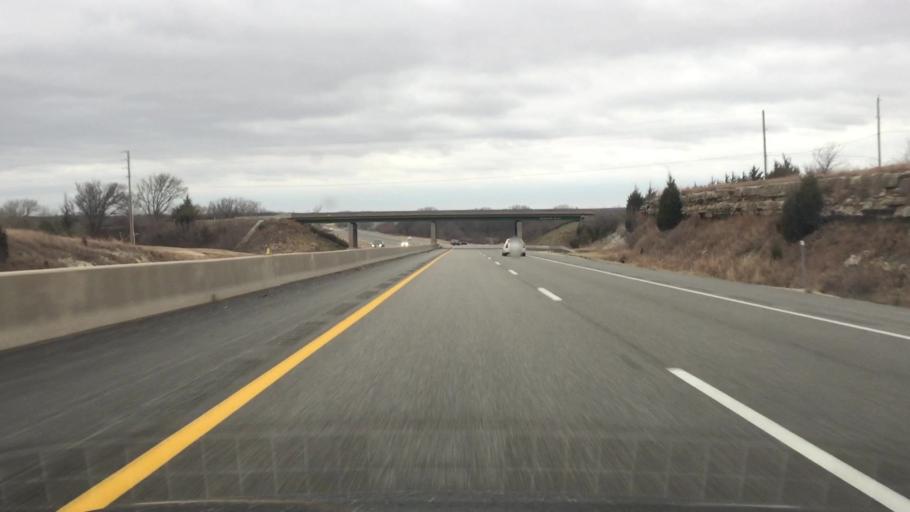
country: US
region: Kansas
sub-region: Butler County
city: Towanda
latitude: 37.7611
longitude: -96.9965
